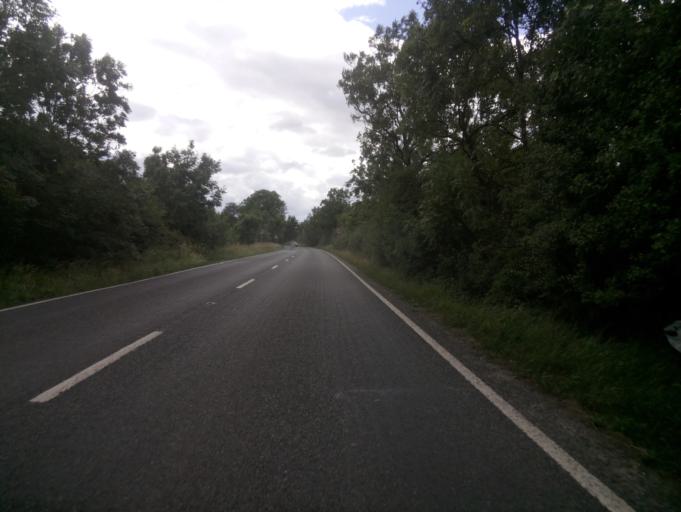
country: GB
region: England
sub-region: Leicestershire
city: Measham
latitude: 52.6532
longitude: -1.5215
